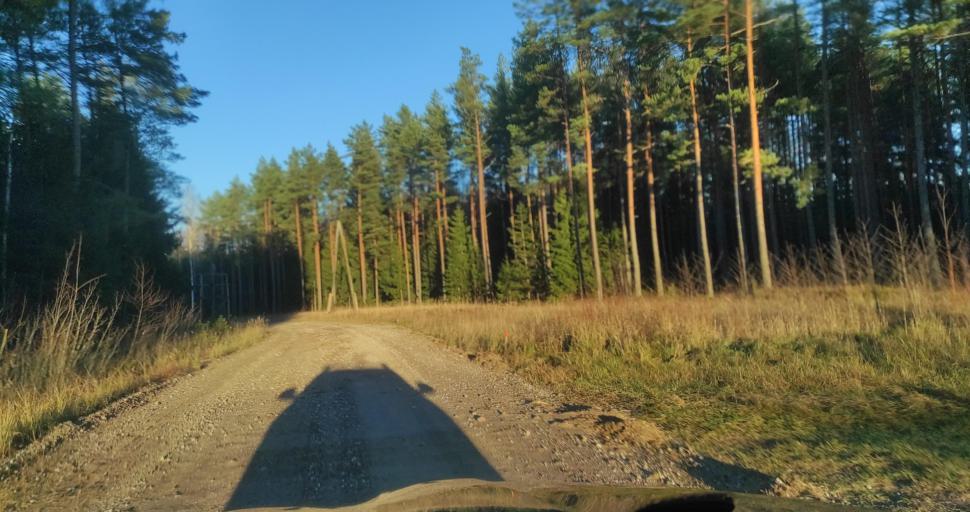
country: LV
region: Dundaga
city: Dundaga
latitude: 57.3729
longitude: 22.0774
